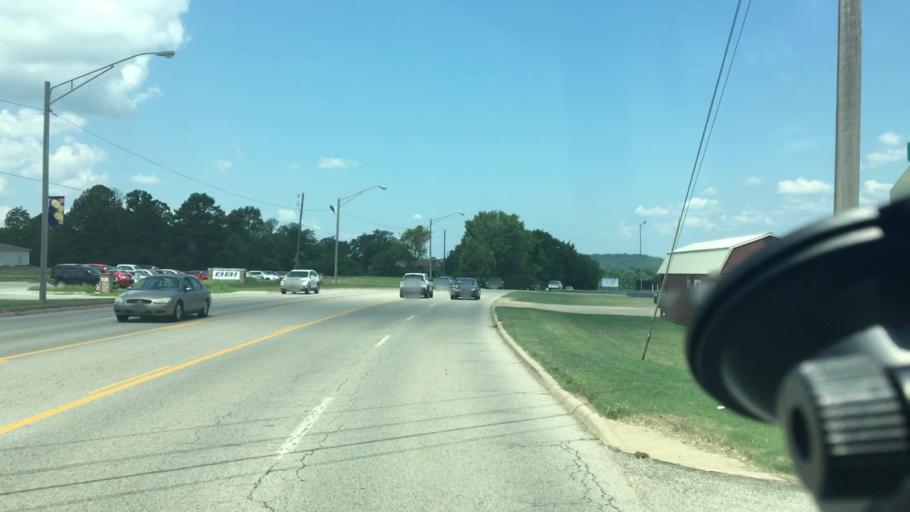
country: US
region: Arkansas
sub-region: Sebastian County
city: Barling
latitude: 35.3372
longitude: -94.3186
